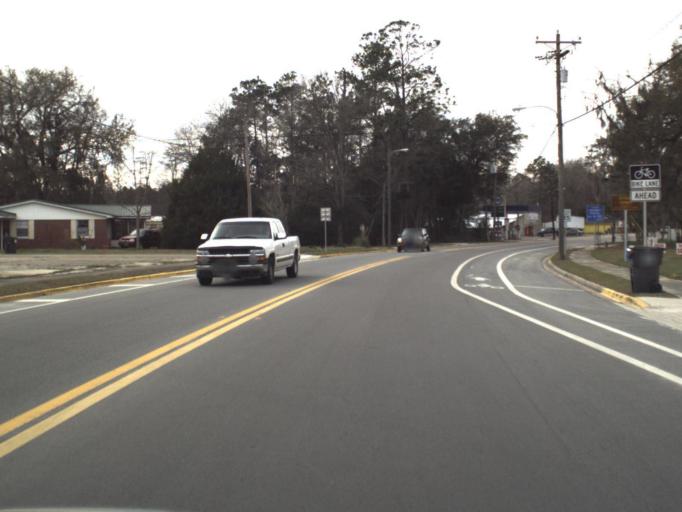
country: US
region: Florida
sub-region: Gulf County
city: Wewahitchka
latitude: 30.1128
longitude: -85.2011
